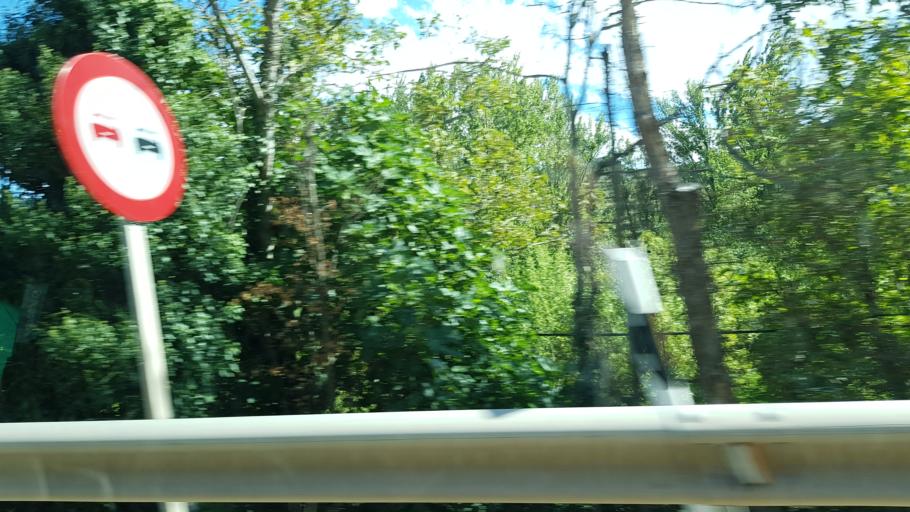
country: ES
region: La Rioja
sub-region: Provincia de La Rioja
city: Viguera
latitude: 42.3121
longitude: -2.5446
